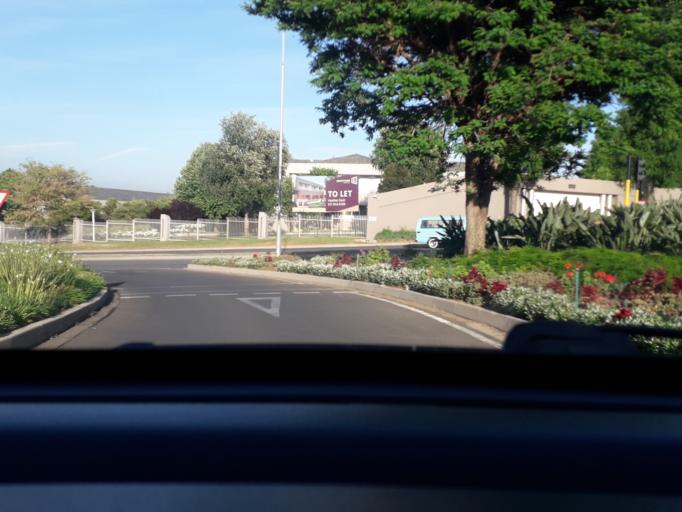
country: ZA
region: Gauteng
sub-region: City of Johannesburg Metropolitan Municipality
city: Midrand
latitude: -26.0585
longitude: 28.0847
